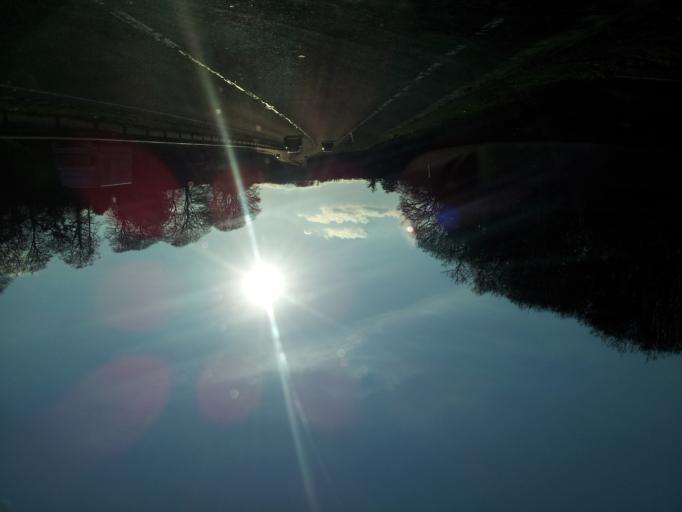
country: GB
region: England
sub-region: Devon
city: Okehampton
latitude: 50.7187
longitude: -4.0347
